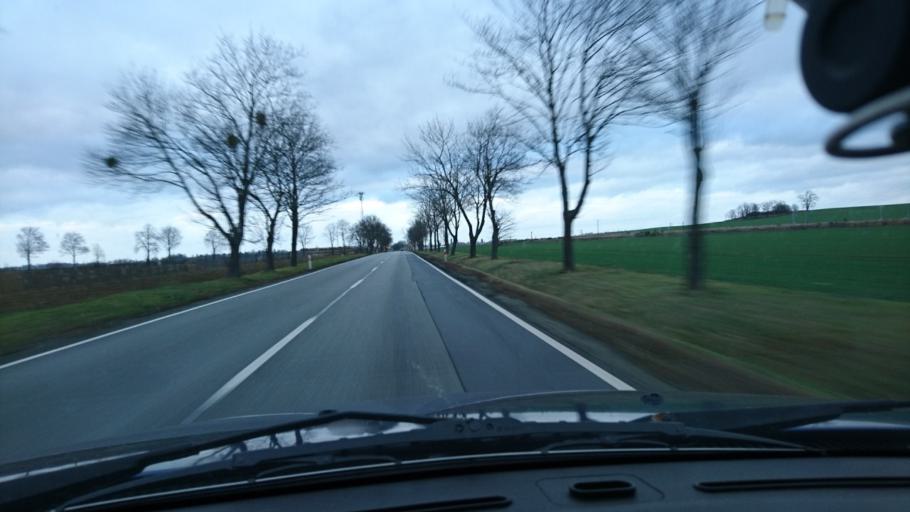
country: PL
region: Opole Voivodeship
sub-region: Powiat kluczborski
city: Byczyna
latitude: 51.0937
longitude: 18.2022
